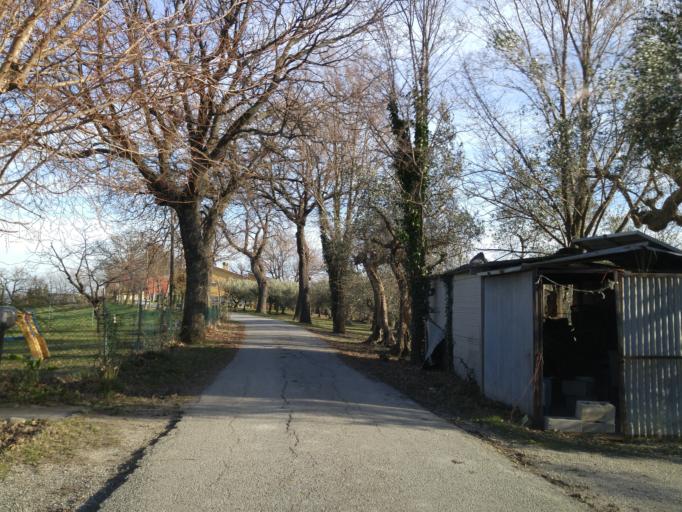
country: IT
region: The Marches
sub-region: Provincia di Pesaro e Urbino
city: Cartoceto
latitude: 43.7782
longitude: 12.8924
